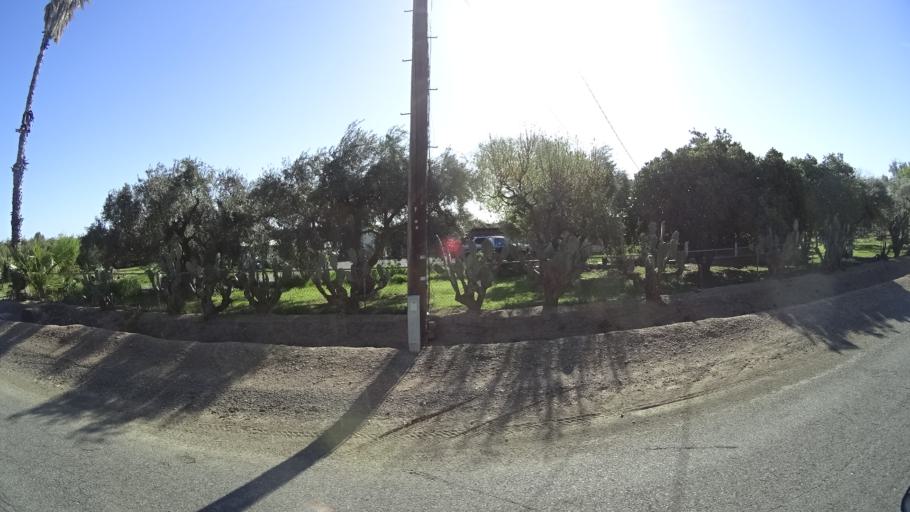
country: US
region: California
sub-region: Glenn County
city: Orland
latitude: 39.7392
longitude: -122.2390
